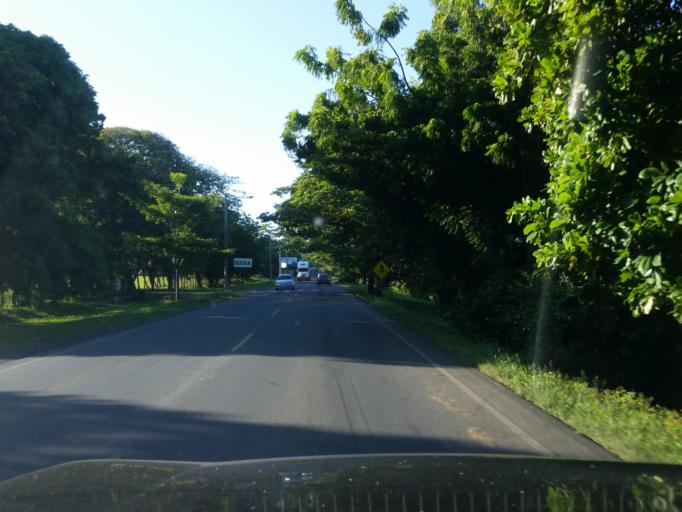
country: NI
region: Rivas
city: Potosi
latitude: 11.4666
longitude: -85.8528
